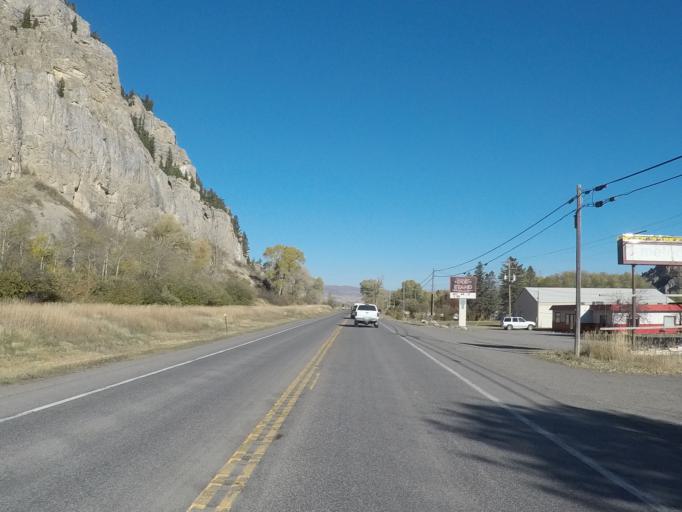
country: US
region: Montana
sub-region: Park County
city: Livingston
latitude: 45.6083
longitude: -110.5760
